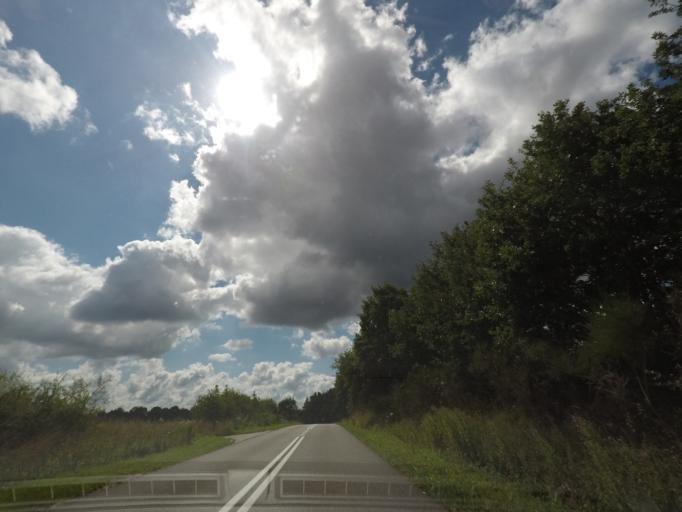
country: PL
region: Pomeranian Voivodeship
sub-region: Powiat wejherowski
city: Leczyce
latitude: 54.5999
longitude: 17.8441
